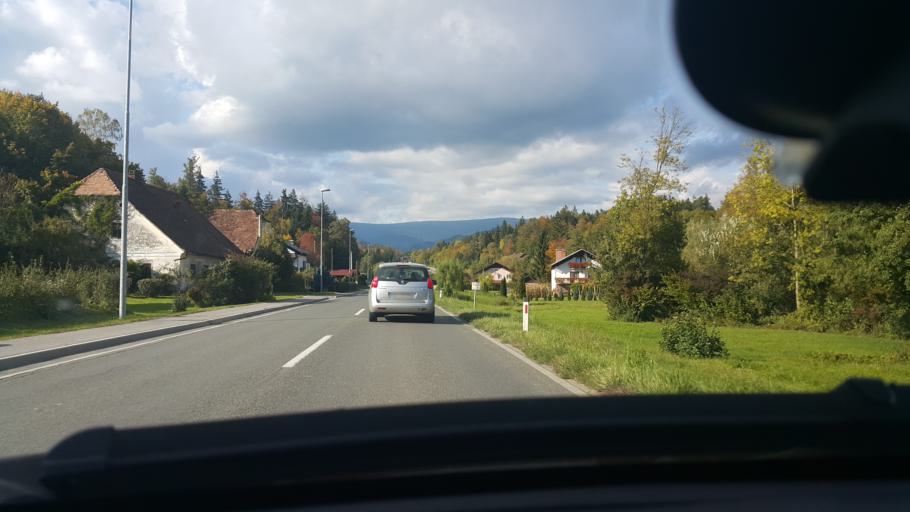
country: SI
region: Zrece
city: Zrece
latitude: 46.3558
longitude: 15.3986
